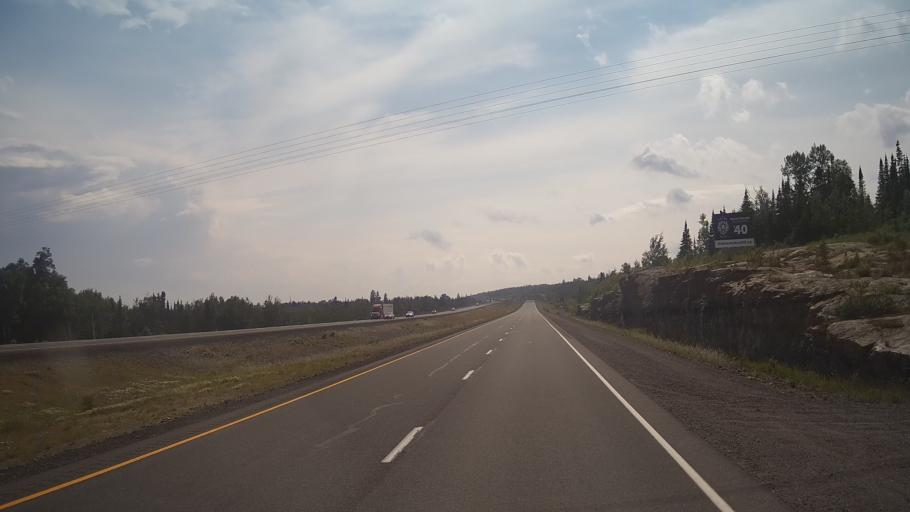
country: CA
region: Ontario
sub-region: Thunder Bay District
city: Thunder Bay
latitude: 48.5570
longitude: -88.8891
